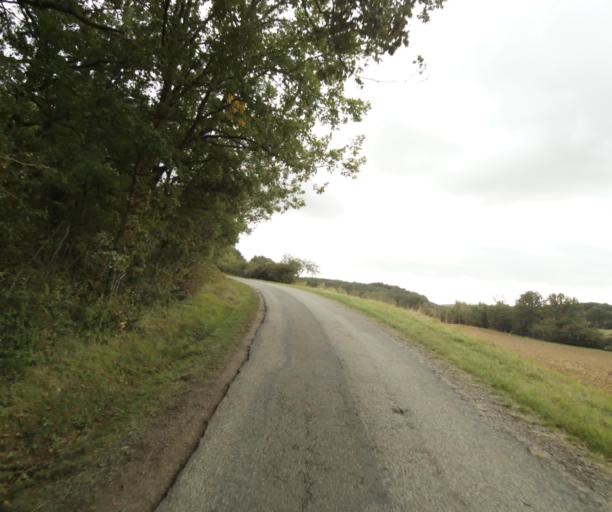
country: FR
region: Midi-Pyrenees
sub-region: Departement du Tarn-et-Garonne
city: Beaumont-de-Lomagne
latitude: 43.8906
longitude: 1.0805
